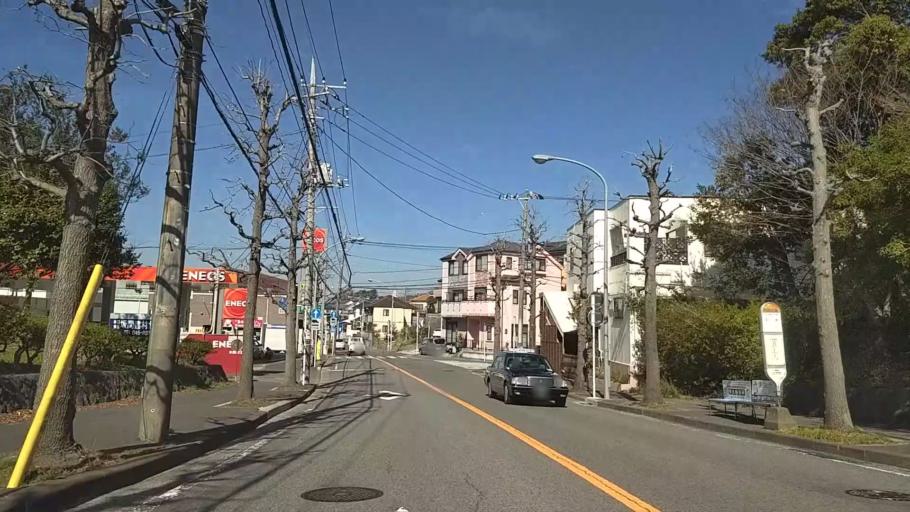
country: JP
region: Kanagawa
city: Kamakura
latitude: 35.3738
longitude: 139.5445
